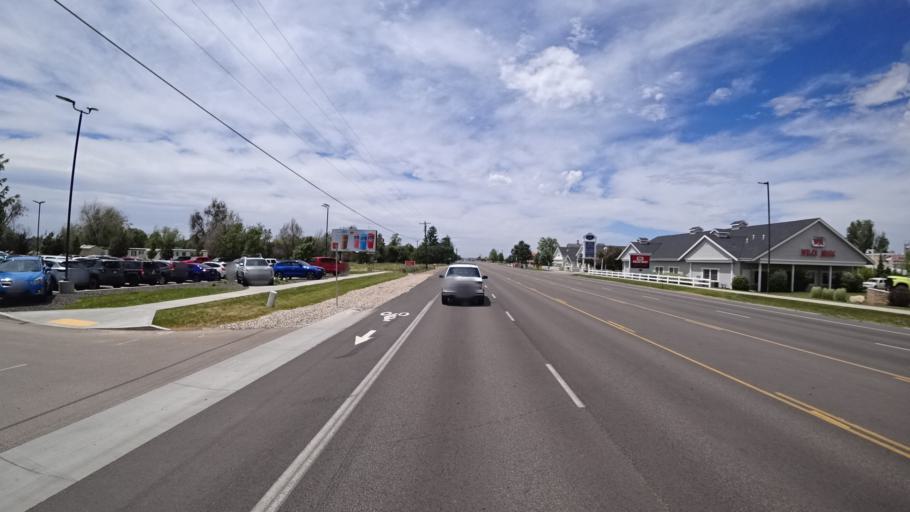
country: US
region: Idaho
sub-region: Ada County
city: Meridian
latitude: 43.6194
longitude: -116.3376
